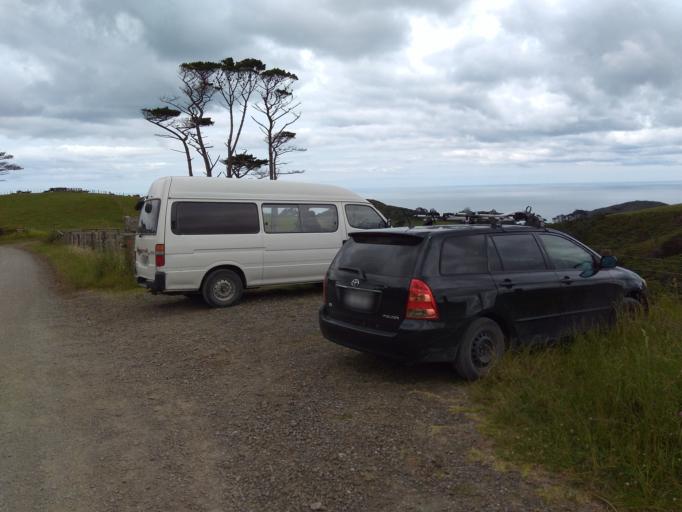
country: NZ
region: Auckland
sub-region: Auckland
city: Muriwai Beach
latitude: -36.9286
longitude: 174.4693
